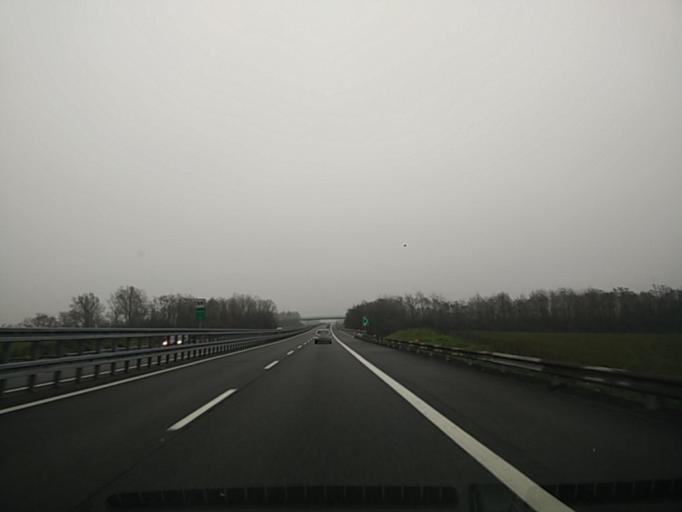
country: IT
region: Piedmont
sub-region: Provincia di Alessandria
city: Felizzano
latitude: 44.9193
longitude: 8.4603
